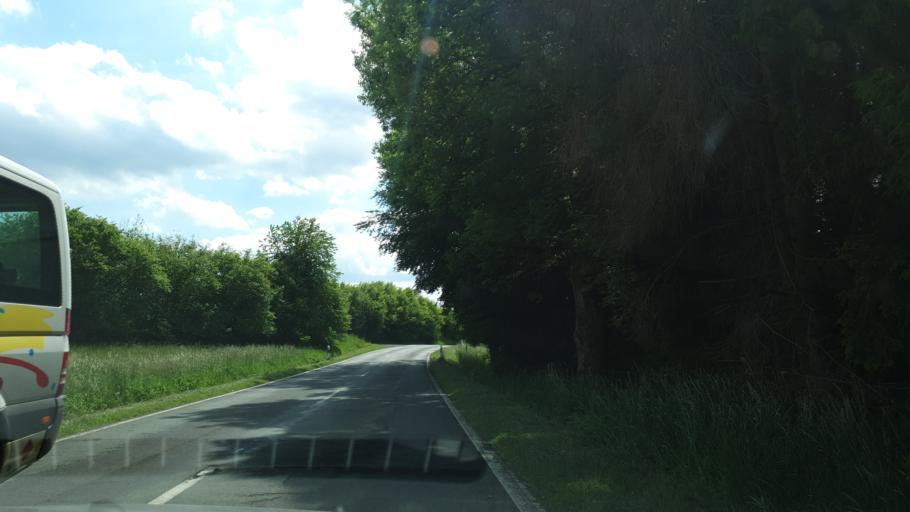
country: DE
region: Rheinland-Pfalz
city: Wolferlingen
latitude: 50.5696
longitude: 7.8601
